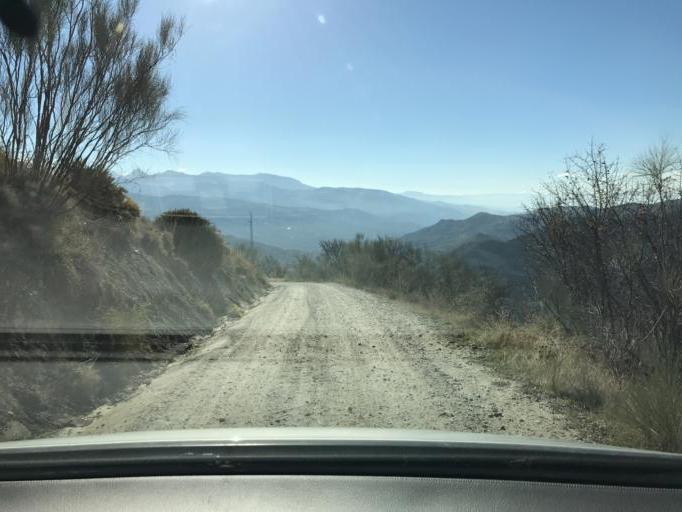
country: ES
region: Andalusia
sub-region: Provincia de Granada
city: Beas de Granada
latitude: 37.2116
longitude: -3.4778
